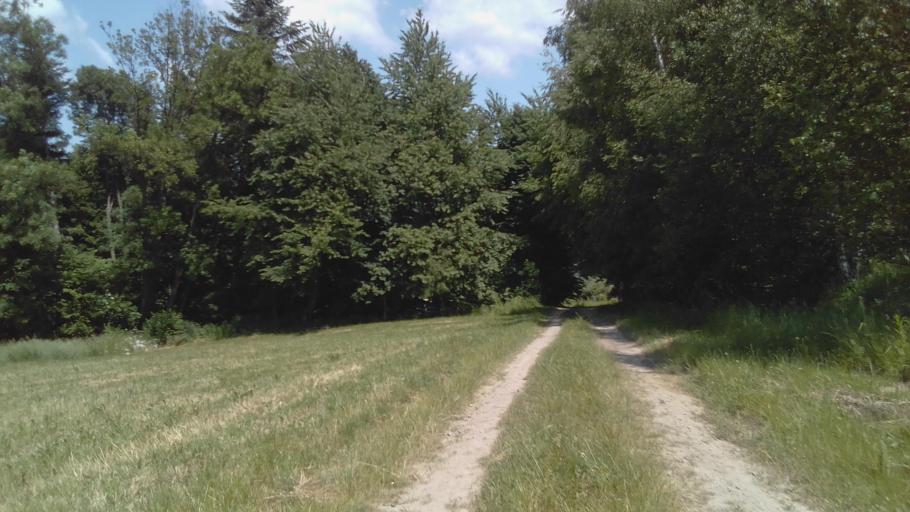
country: PL
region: Subcarpathian Voivodeship
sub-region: Powiat strzyzowski
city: Wysoka Strzyzowska
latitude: 49.8604
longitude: 21.7591
